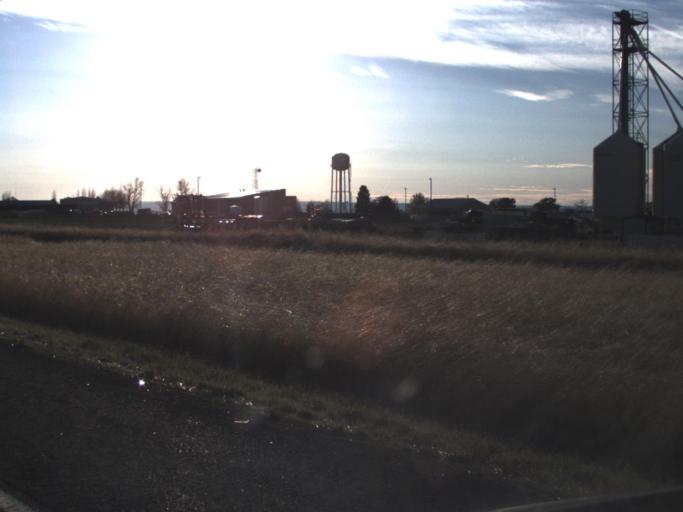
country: US
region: Washington
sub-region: Walla Walla County
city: Walla Walla East
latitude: 46.0933
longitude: -118.2564
